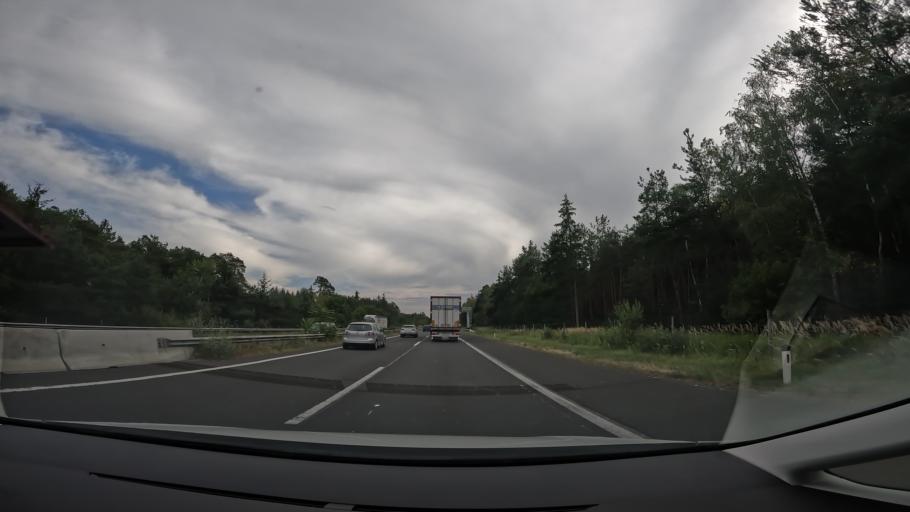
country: AT
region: Styria
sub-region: Politischer Bezirk Hartberg-Fuerstenfeld
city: Hainersdorf
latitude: 47.1105
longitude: 15.9844
